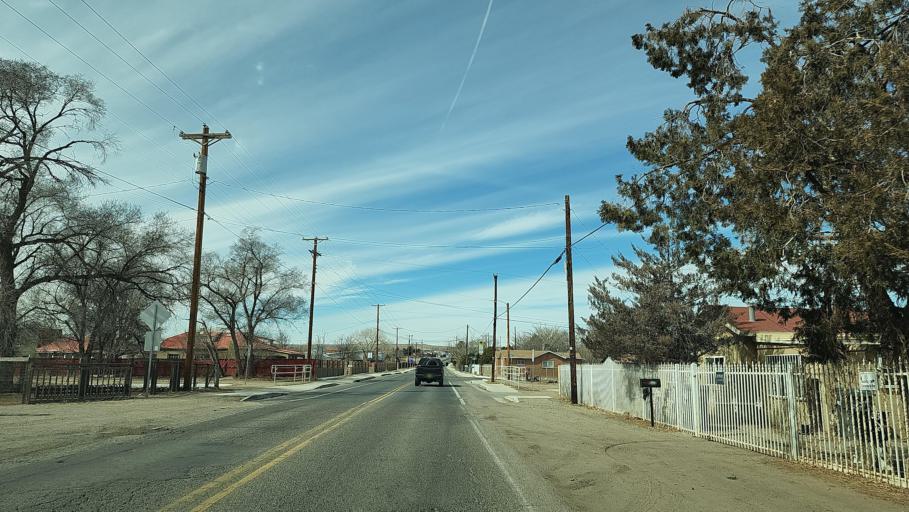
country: US
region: New Mexico
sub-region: Bernalillo County
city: South Valley
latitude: 35.0361
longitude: -106.7073
